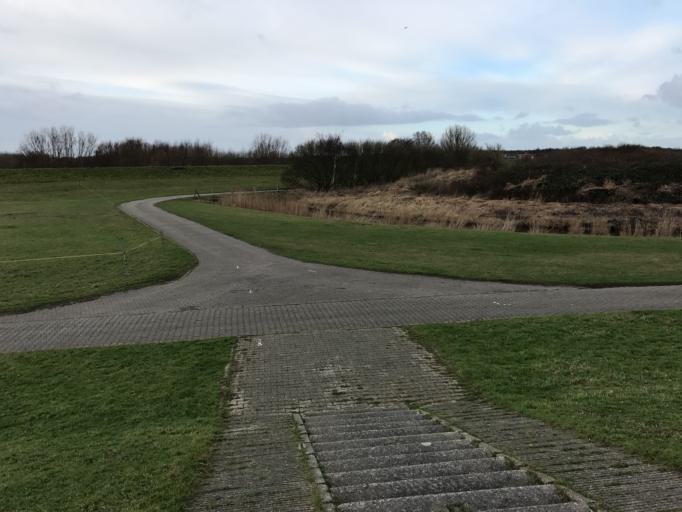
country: DE
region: Lower Saxony
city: Borkum
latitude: 53.5831
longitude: 6.7162
